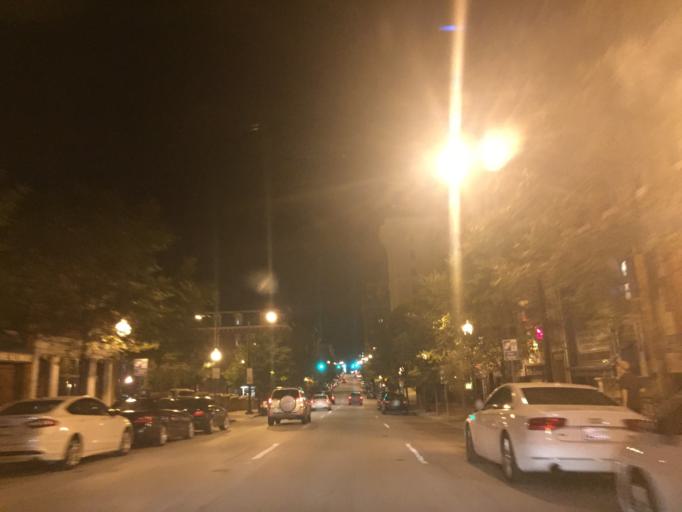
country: US
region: Maryland
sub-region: City of Baltimore
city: Baltimore
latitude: 39.2988
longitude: -76.6158
